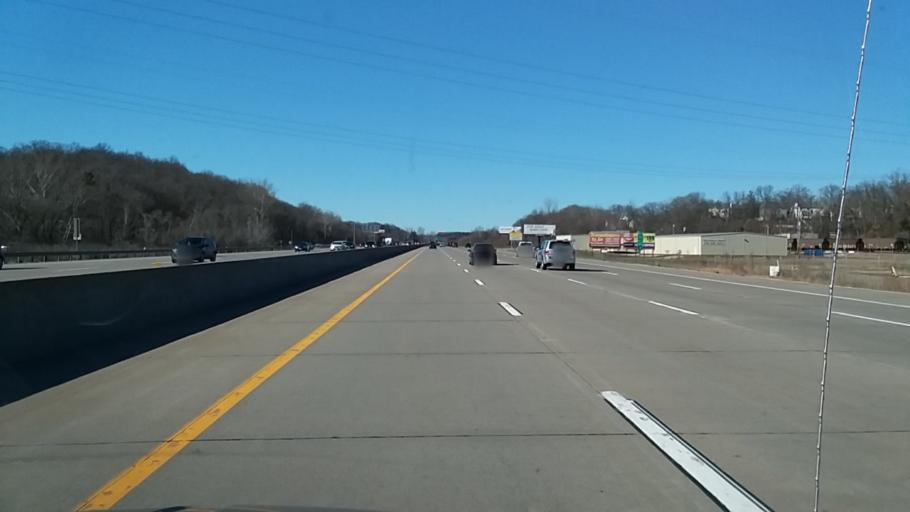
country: US
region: Missouri
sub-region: Jefferson County
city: Imperial
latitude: 38.3837
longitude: -90.3808
